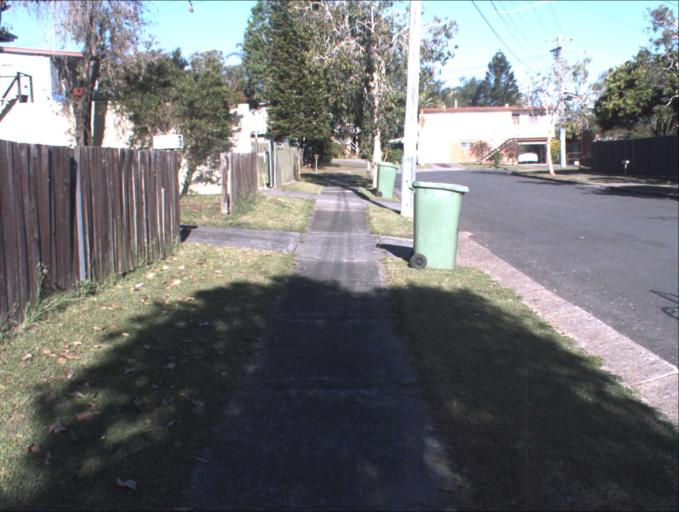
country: AU
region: Queensland
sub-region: Logan
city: Logan City
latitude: -27.6401
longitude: 153.1152
